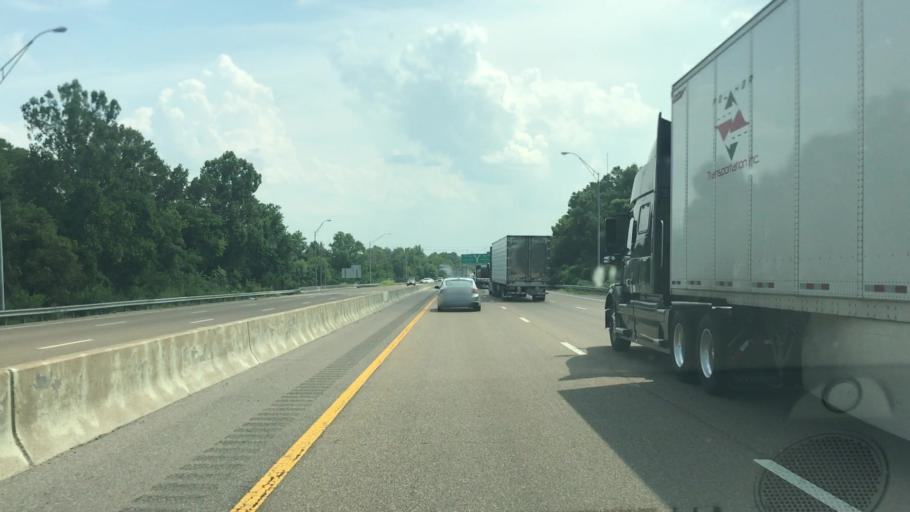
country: US
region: Tennessee
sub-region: Shelby County
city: Memphis
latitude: 35.1719
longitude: -90.0185
